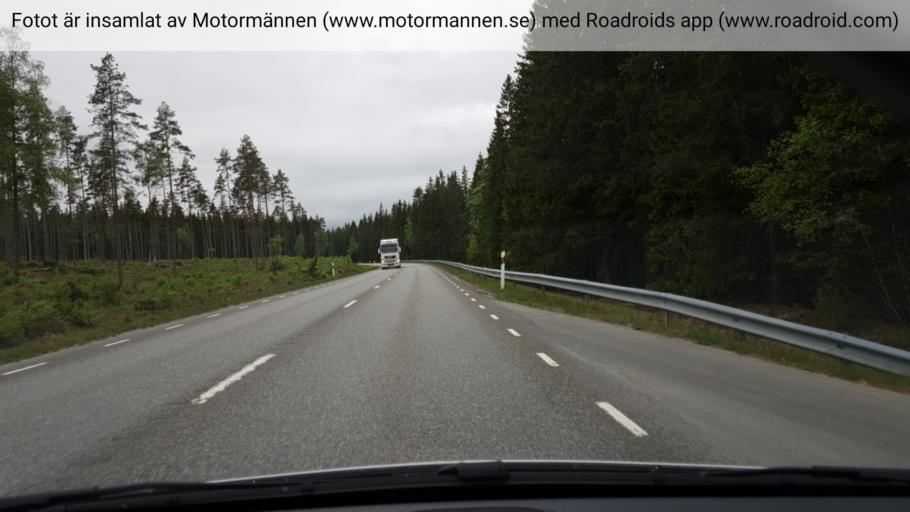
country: SE
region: Joenkoeping
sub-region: Gnosjo Kommun
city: Marieholm
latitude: 57.6308
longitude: 13.7808
